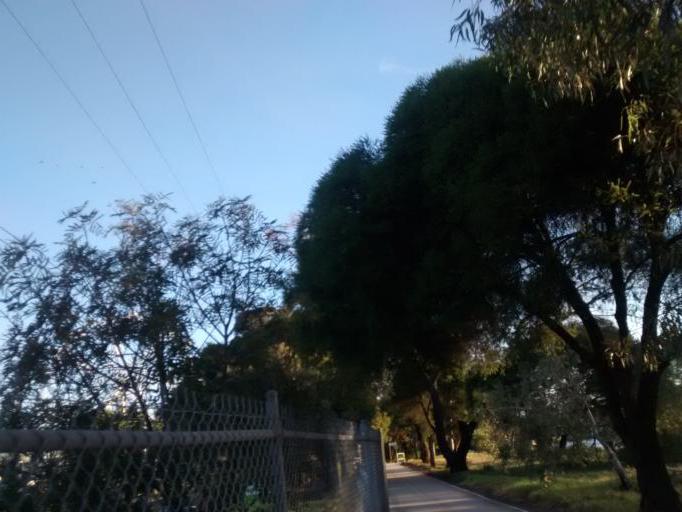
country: AU
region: Victoria
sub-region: Melbourne
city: North Melbourne
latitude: -37.8077
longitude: 144.9362
